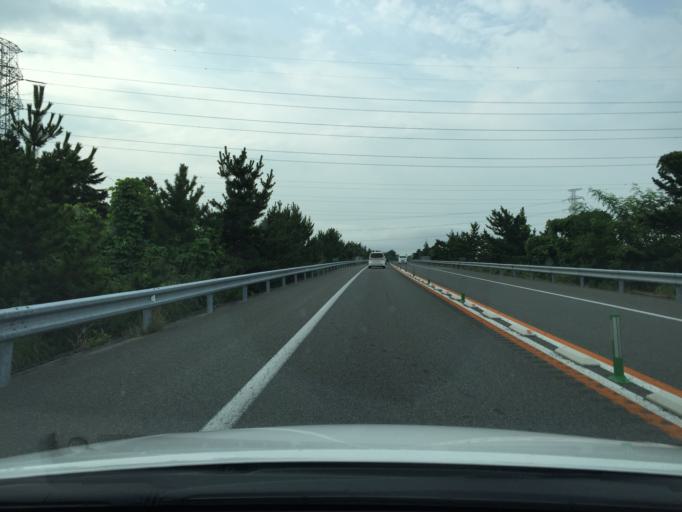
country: JP
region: Fukushima
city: Namie
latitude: 37.3614
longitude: 140.9706
